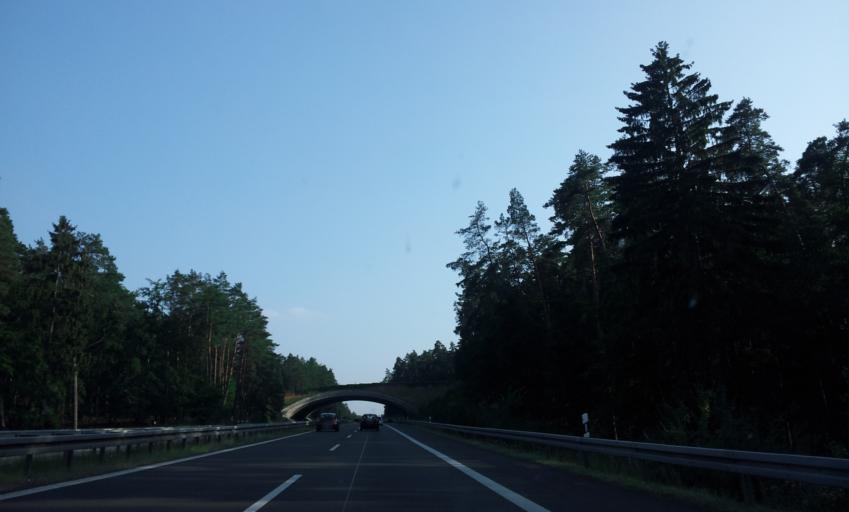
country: DE
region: Brandenburg
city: Althuttendorf
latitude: 53.0648
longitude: 13.8410
